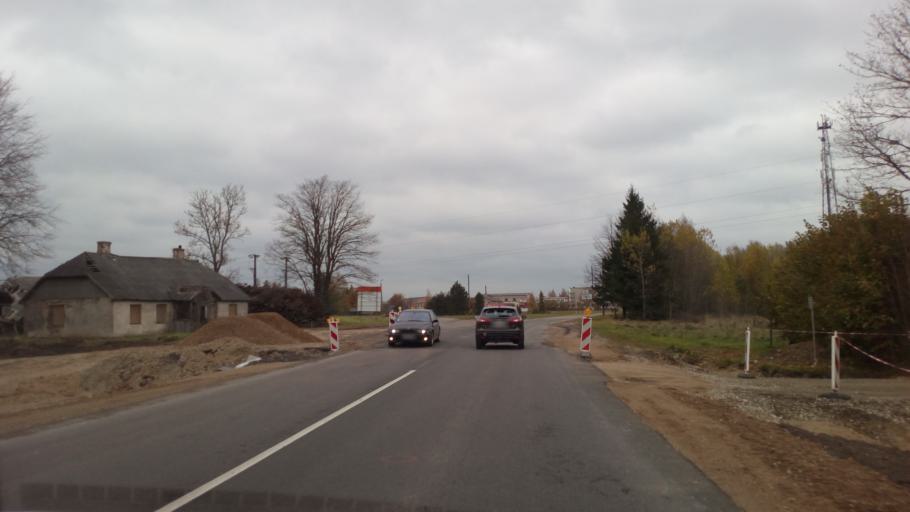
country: LV
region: Talsu Rajons
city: Talsi
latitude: 57.2309
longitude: 22.5855
